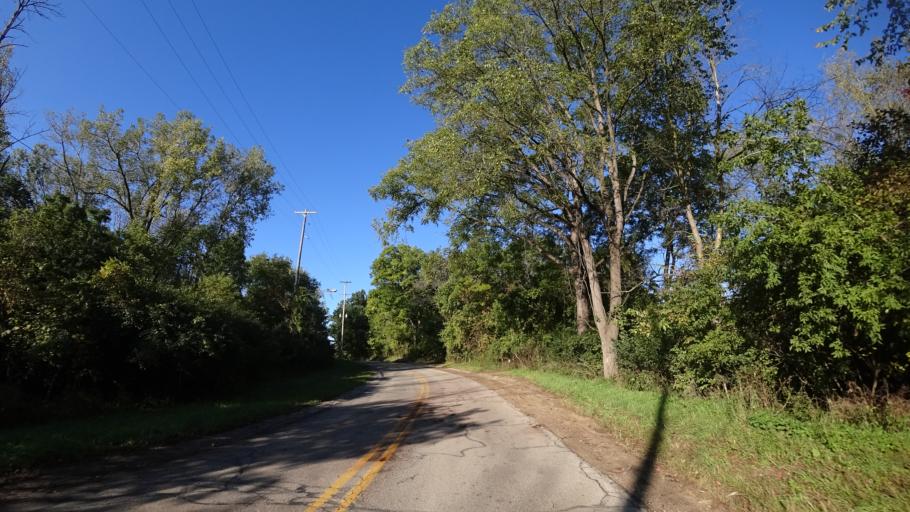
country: US
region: Michigan
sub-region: Kent County
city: Wyoming
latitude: 42.9462
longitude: -85.7245
